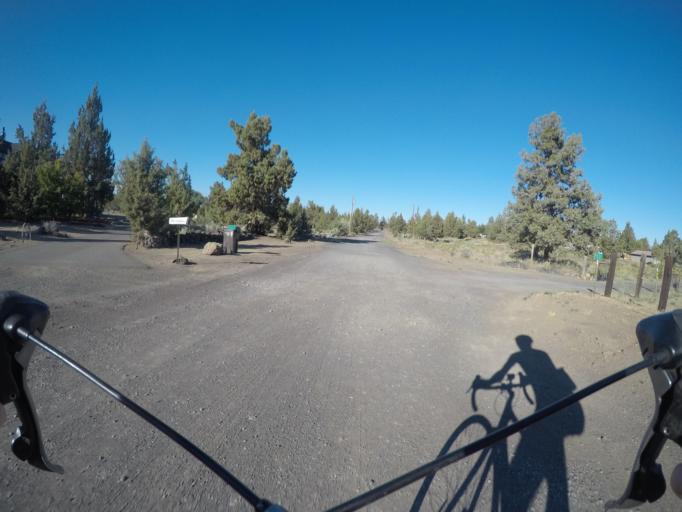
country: US
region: Oregon
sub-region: Deschutes County
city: Redmond
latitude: 44.2242
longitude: -121.2333
